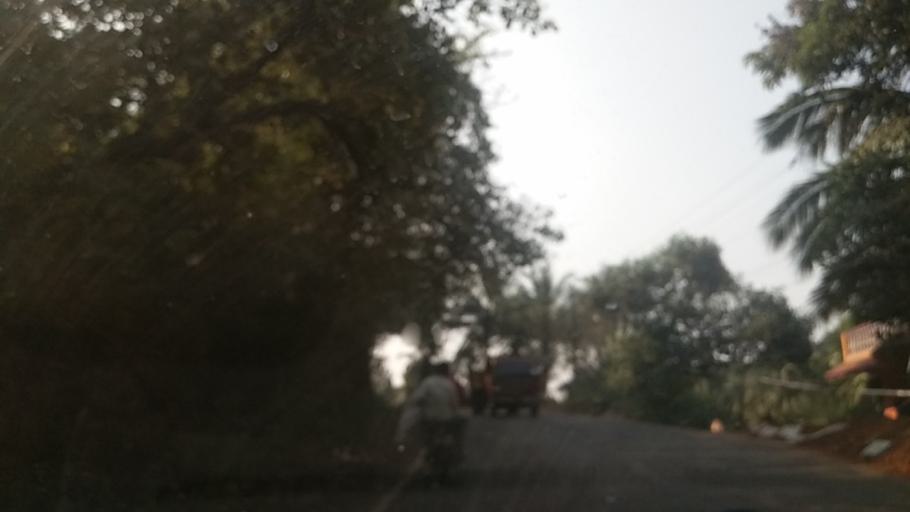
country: IN
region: Goa
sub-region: North Goa
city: Pernem
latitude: 15.7156
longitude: 73.8050
